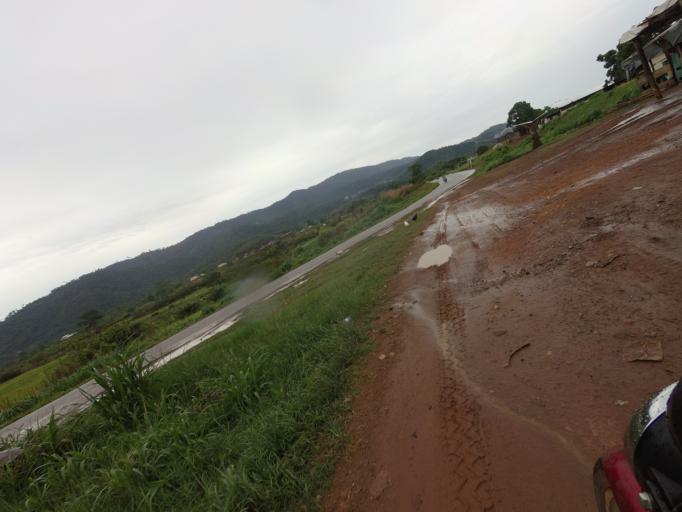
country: LR
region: Nimba
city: New Yekepa
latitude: 7.5714
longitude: -8.5463
